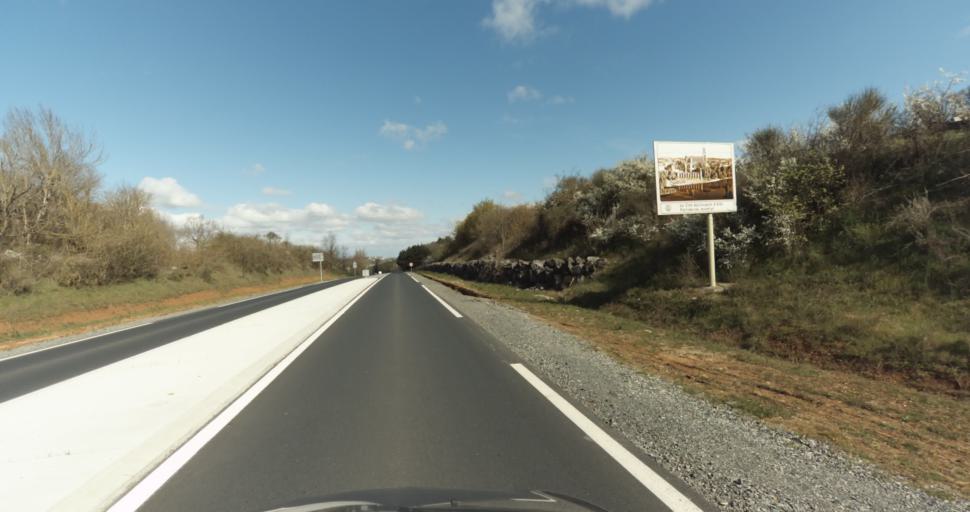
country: FR
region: Midi-Pyrenees
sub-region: Departement du Tarn
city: Puygouzon
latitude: 43.8655
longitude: 2.1869
